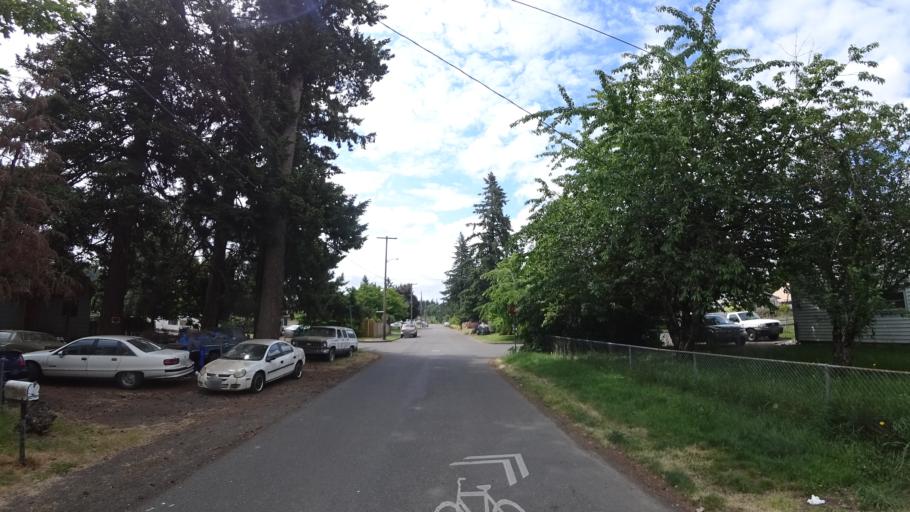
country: US
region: Oregon
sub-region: Multnomah County
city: Lents
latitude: 45.4934
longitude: -122.5275
